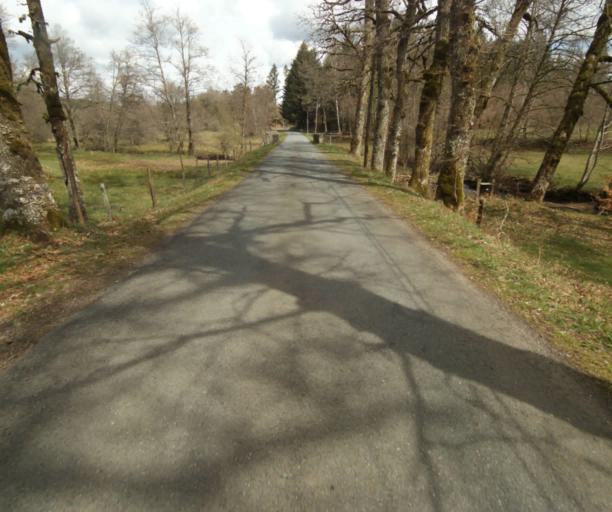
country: FR
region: Limousin
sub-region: Departement de la Correze
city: Correze
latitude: 45.3811
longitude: 1.9543
